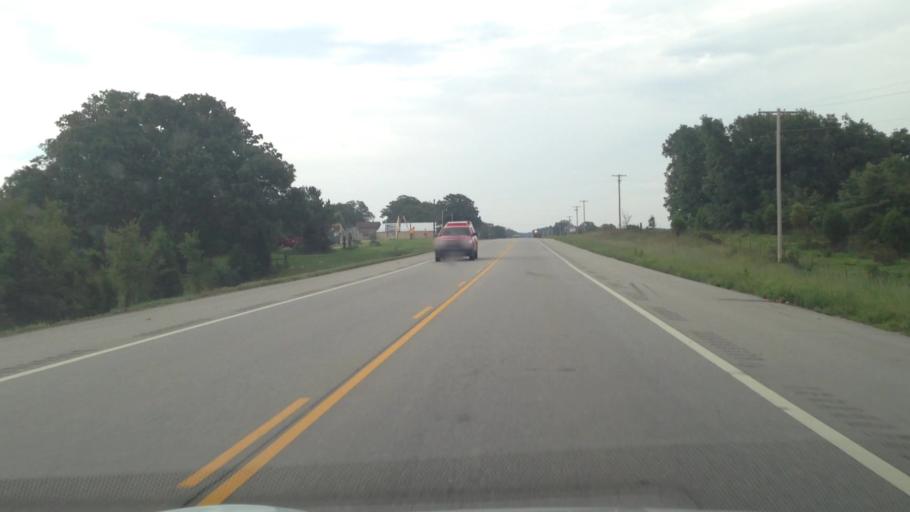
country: US
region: Kansas
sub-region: Cherokee County
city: Galena
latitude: 37.0236
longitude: -94.6562
